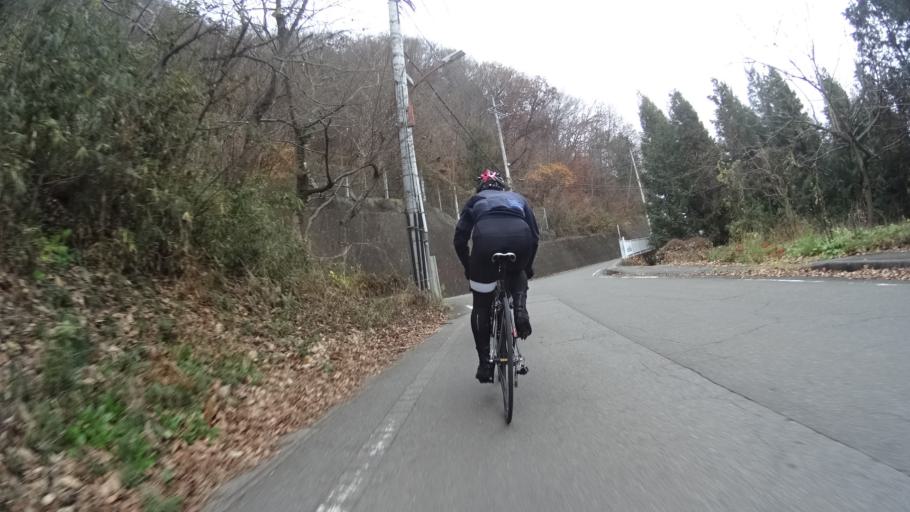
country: JP
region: Yamanashi
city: Otsuki
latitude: 35.6040
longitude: 138.9358
